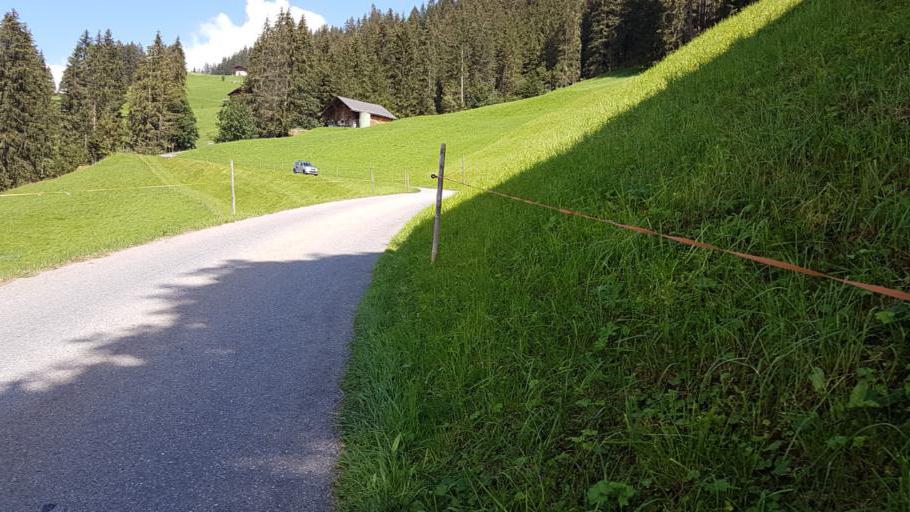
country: CH
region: Bern
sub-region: Frutigen-Niedersimmental District
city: Adelboden
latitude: 46.5024
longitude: 7.5882
